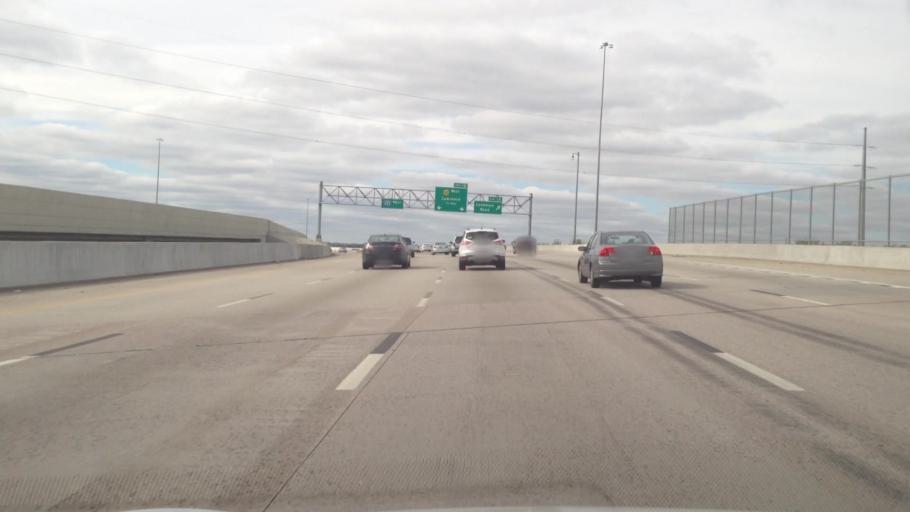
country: US
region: Kansas
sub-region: Johnson County
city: Lenexa
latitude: 38.9412
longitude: -94.7512
